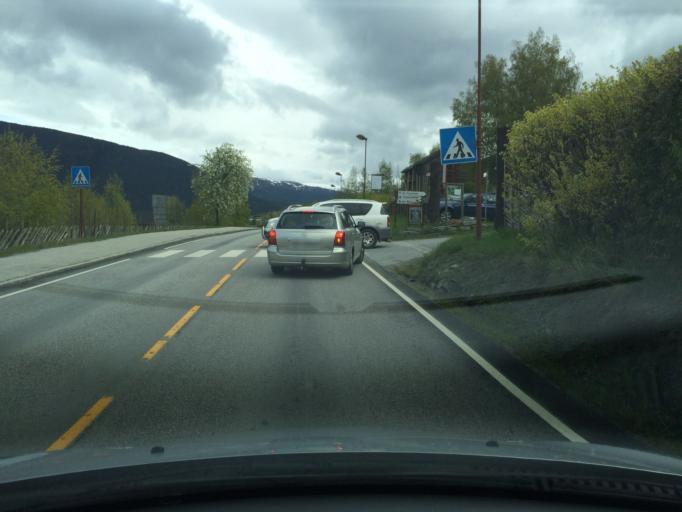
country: NO
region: Oppland
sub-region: Lom
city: Fossbergom
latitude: 61.8387
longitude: 8.5723
